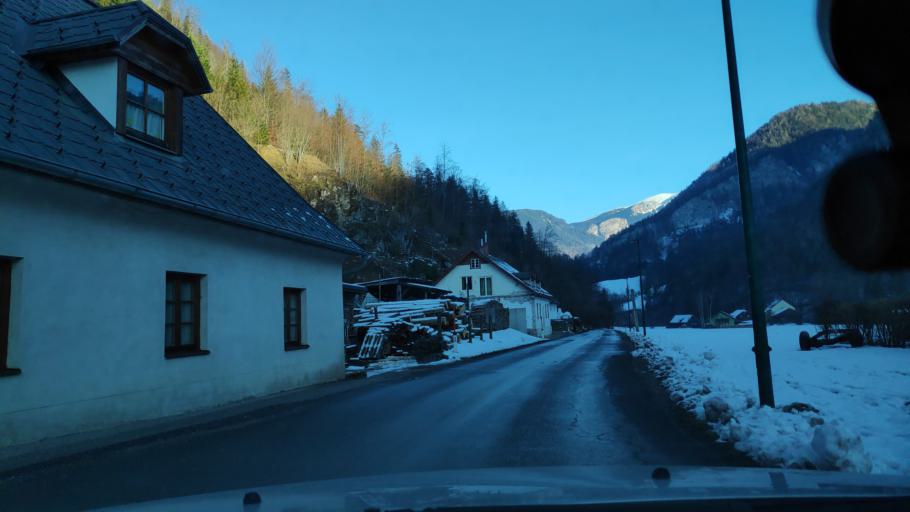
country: AT
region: Lower Austria
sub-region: Politischer Bezirk Neunkirchen
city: Schwarzau im Gebirge
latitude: 47.7641
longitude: 15.6974
